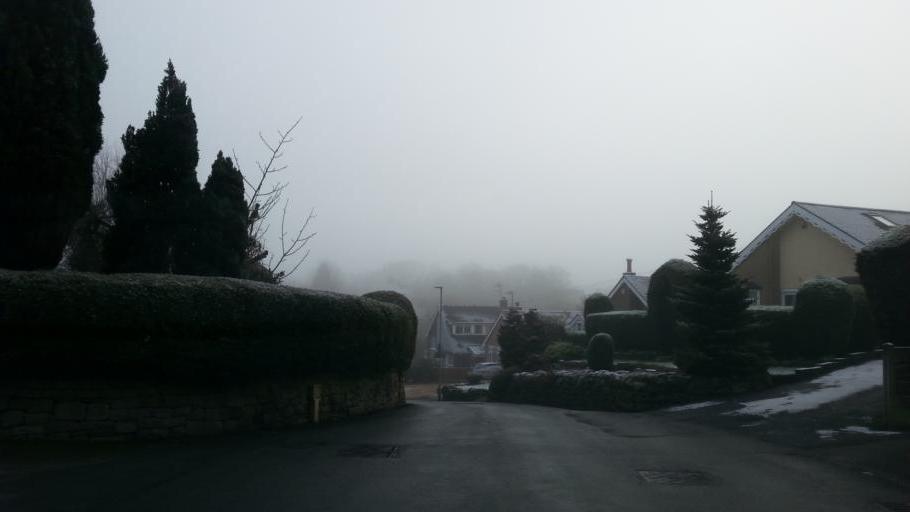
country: GB
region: England
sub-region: Staffordshire
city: Biddulph
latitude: 53.1242
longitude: -2.1731
